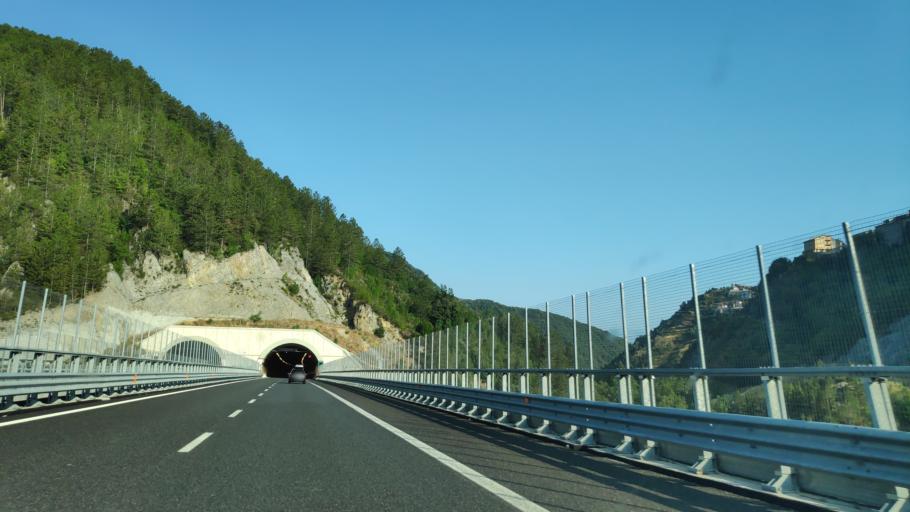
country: IT
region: Calabria
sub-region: Provincia di Cosenza
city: Mormanno
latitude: 39.8795
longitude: 15.9882
